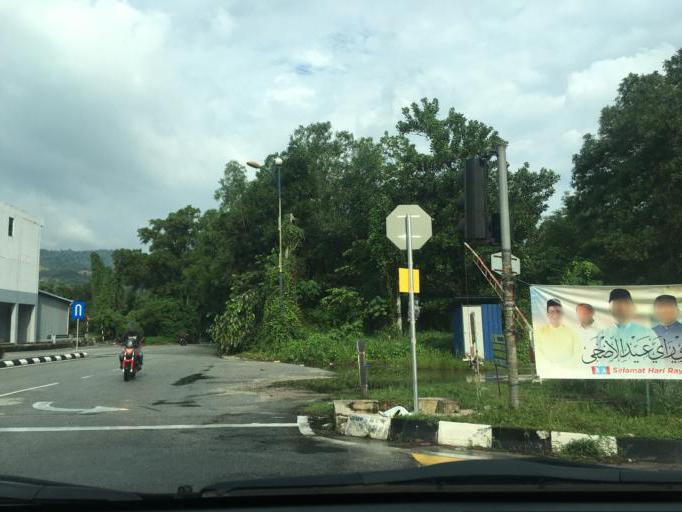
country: MY
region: Selangor
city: Rawang
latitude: 3.3212
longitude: 101.5797
